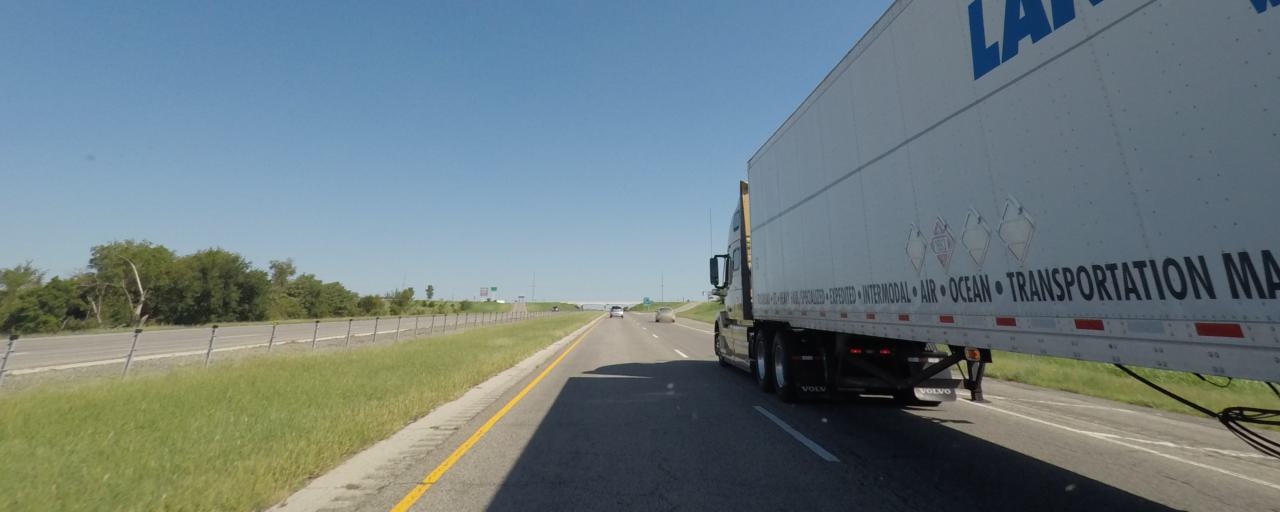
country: US
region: Oklahoma
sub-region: Noble County
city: Perry
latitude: 36.2704
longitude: -97.3276
